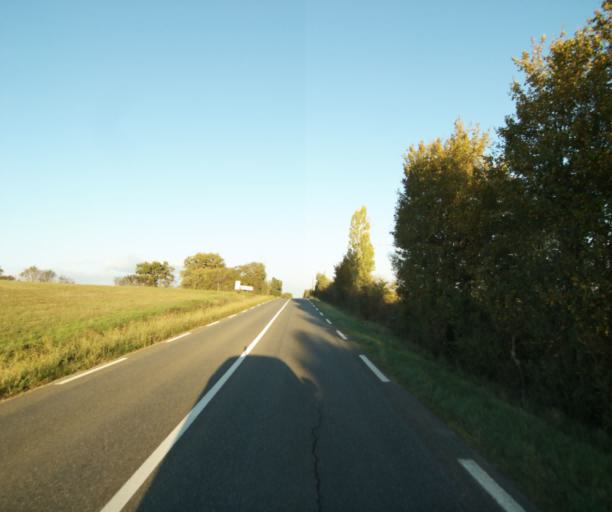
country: FR
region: Midi-Pyrenees
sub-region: Departement du Gers
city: Vic-Fezensac
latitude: 43.7599
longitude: 0.1979
